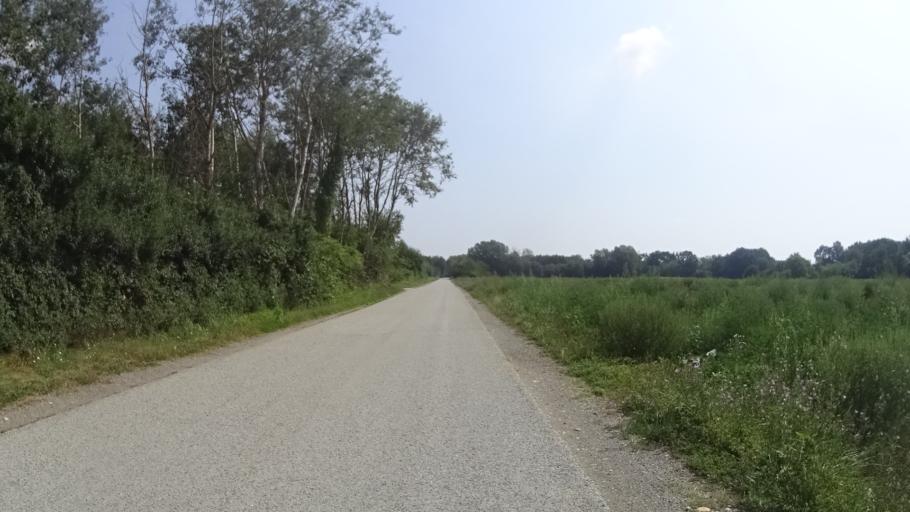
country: HR
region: Medimurska
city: Hodosan
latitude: 46.3951
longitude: 16.6174
